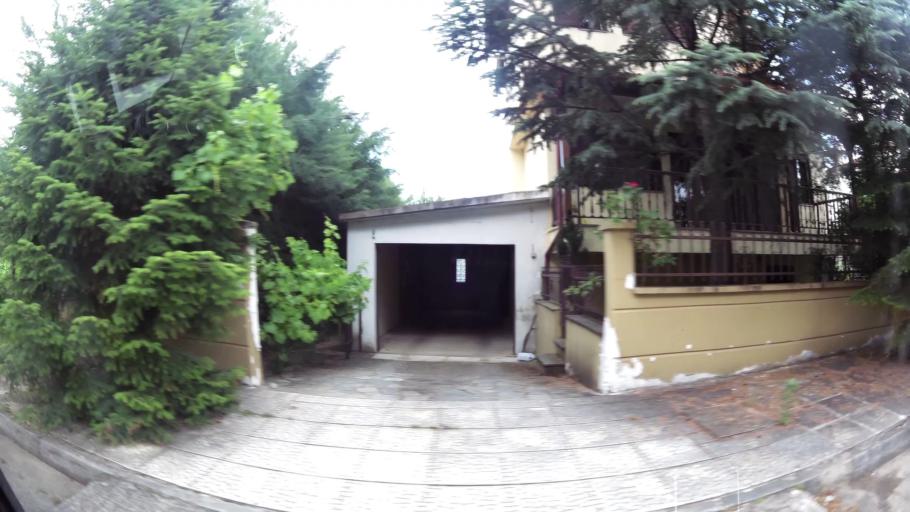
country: GR
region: West Macedonia
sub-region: Nomos Kozanis
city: Koila
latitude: 40.3220
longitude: 21.8232
